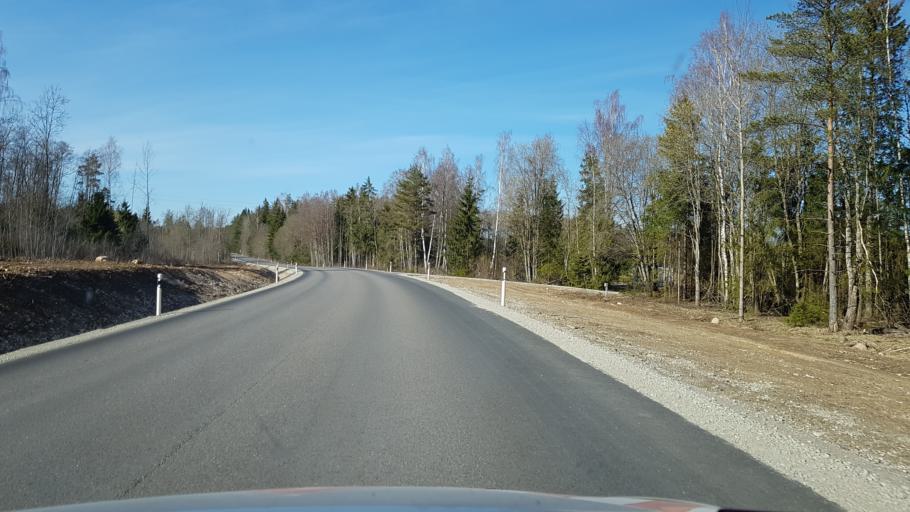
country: EE
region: Laeaene-Virumaa
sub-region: Vinni vald
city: Vinni
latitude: 59.1184
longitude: 26.6179
